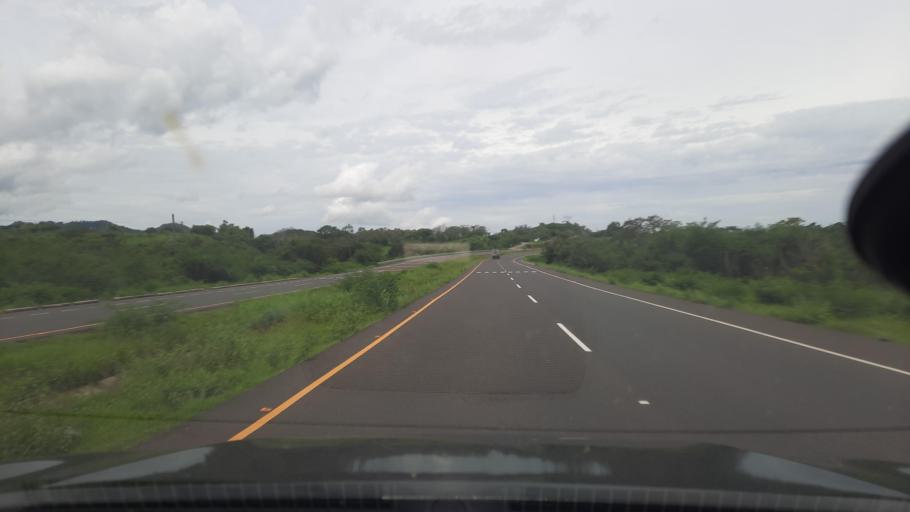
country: HN
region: Valle
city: Aramecina
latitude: 13.7784
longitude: -87.6994
